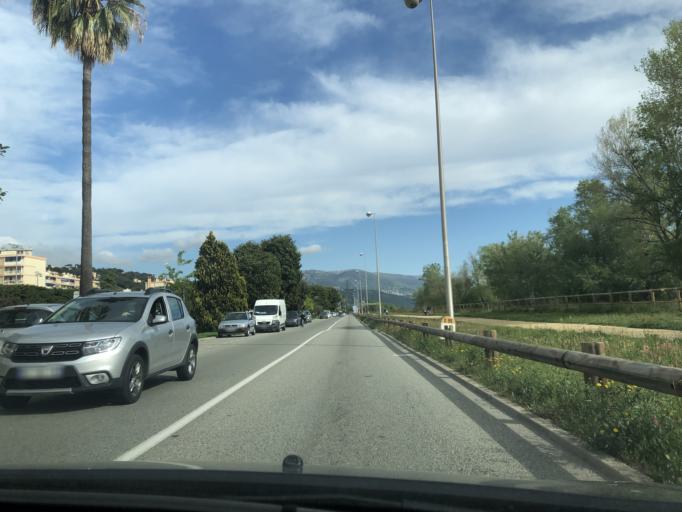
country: FR
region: Provence-Alpes-Cote d'Azur
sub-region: Departement des Alpes-Maritimes
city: Saint-Laurent-du-Var
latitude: 43.6791
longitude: 7.1907
